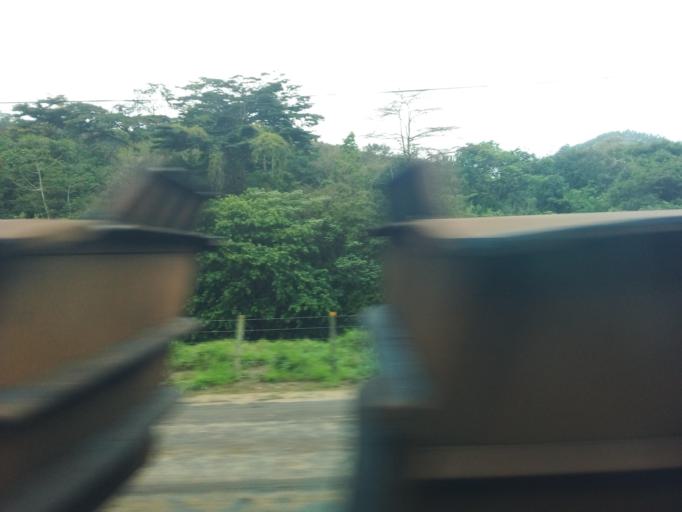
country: BR
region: Minas Gerais
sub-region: Rio Piracicaba
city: Rio Piracicaba
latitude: -19.9475
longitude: -43.1870
